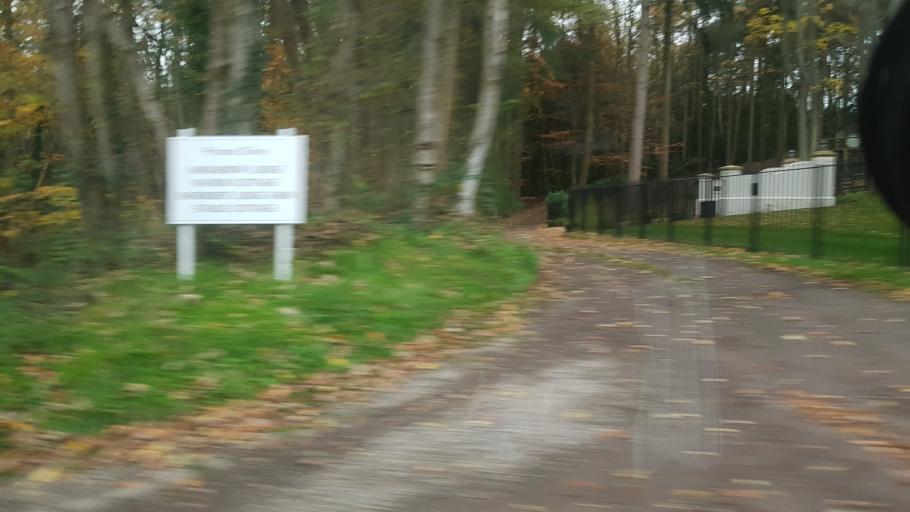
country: GB
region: England
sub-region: Hampshire
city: Yateley
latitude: 51.3578
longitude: -0.8229
